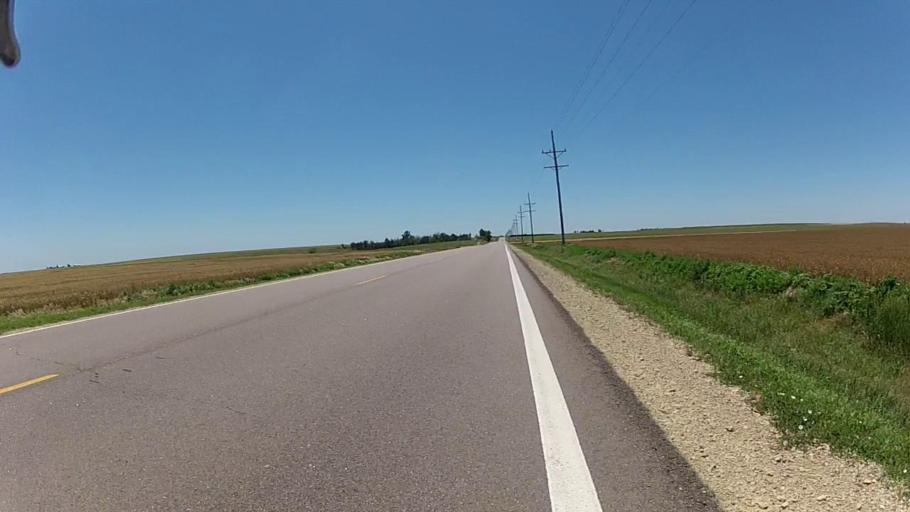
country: US
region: Kansas
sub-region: Kiowa County
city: Greensburg
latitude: 37.5441
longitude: -99.3210
